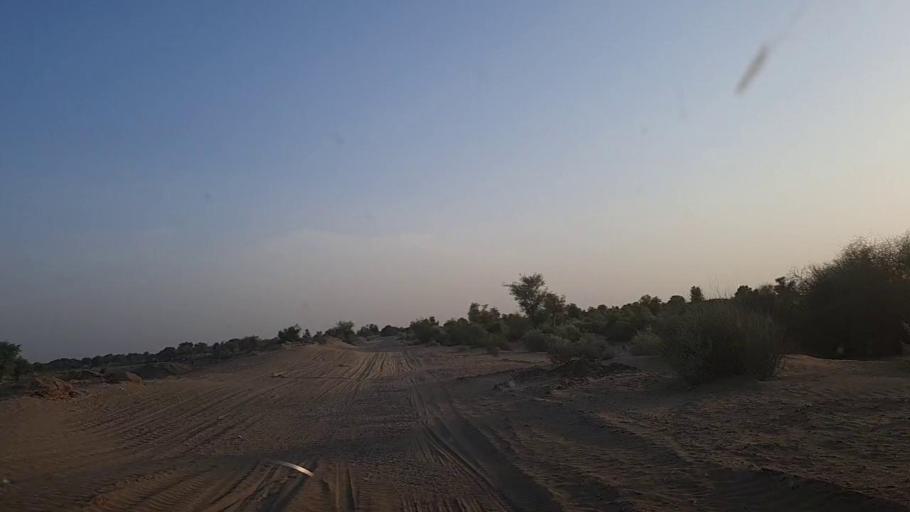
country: PK
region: Sindh
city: Khanpur
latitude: 27.6164
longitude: 69.4411
